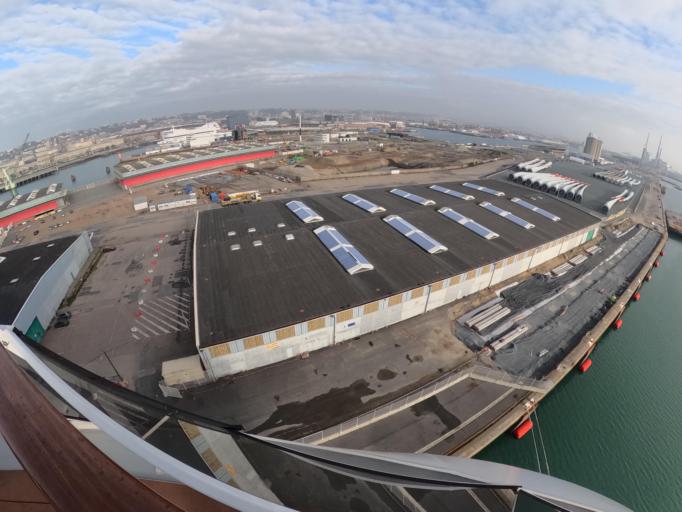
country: FR
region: Haute-Normandie
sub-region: Departement de la Seine-Maritime
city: Le Havre
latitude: 49.4799
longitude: 0.1106
